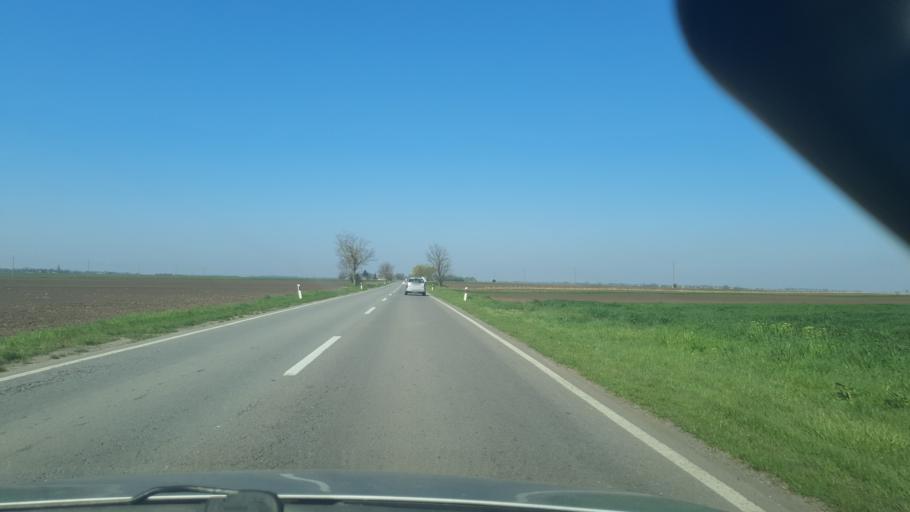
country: RS
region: Autonomna Pokrajina Vojvodina
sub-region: Zapadnobacki Okrug
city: Sombor
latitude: 45.7680
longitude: 19.2297
